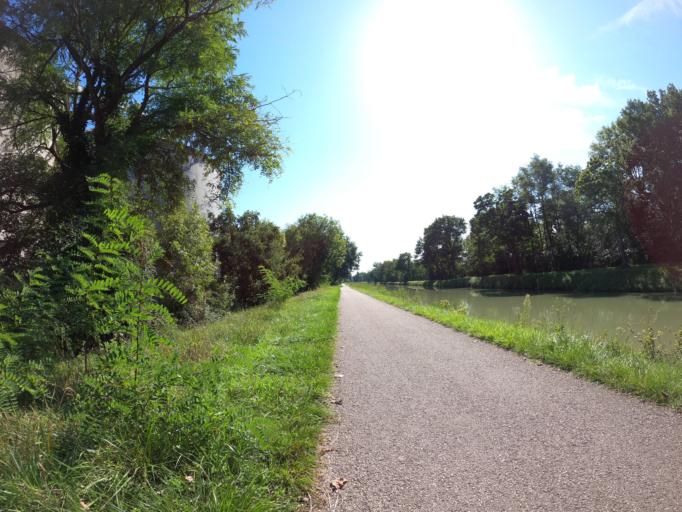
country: FR
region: Midi-Pyrenees
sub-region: Departement du Tarn-et-Garonne
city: Montech
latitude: 43.9557
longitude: 1.2438
